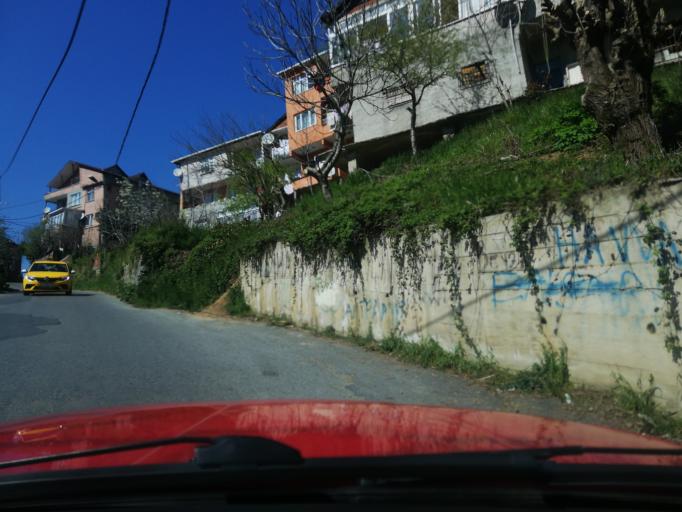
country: TR
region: Istanbul
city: Mahmut Sevket Pasa
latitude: 41.1133
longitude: 29.1125
